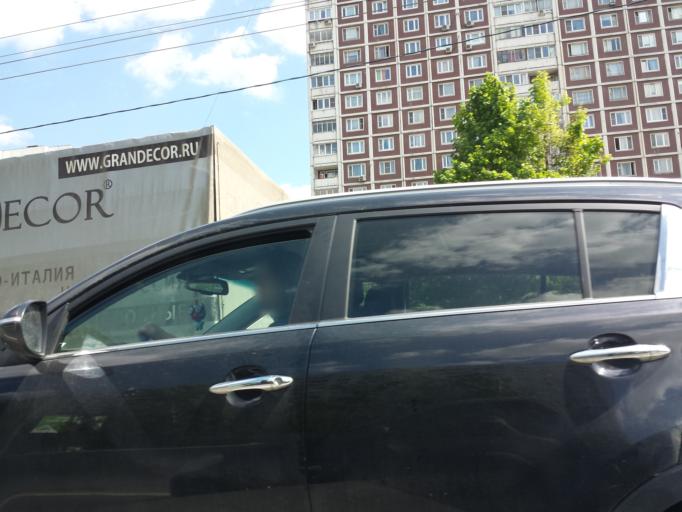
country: RU
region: Moscow
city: Lianozovo
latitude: 55.9032
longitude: 37.5872
